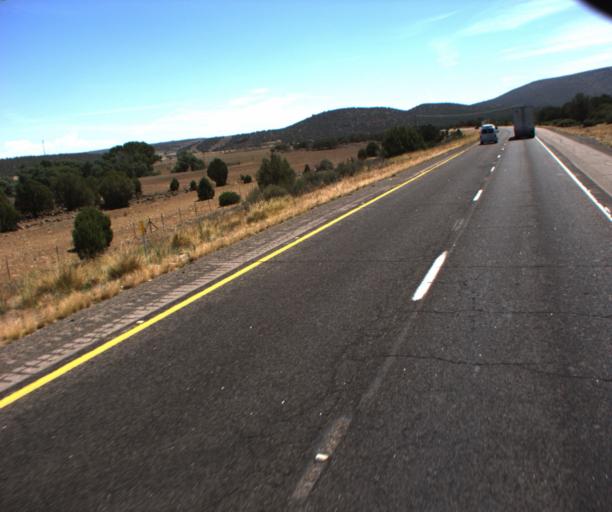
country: US
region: Arizona
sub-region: Mohave County
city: Peach Springs
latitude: 35.1810
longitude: -113.4632
